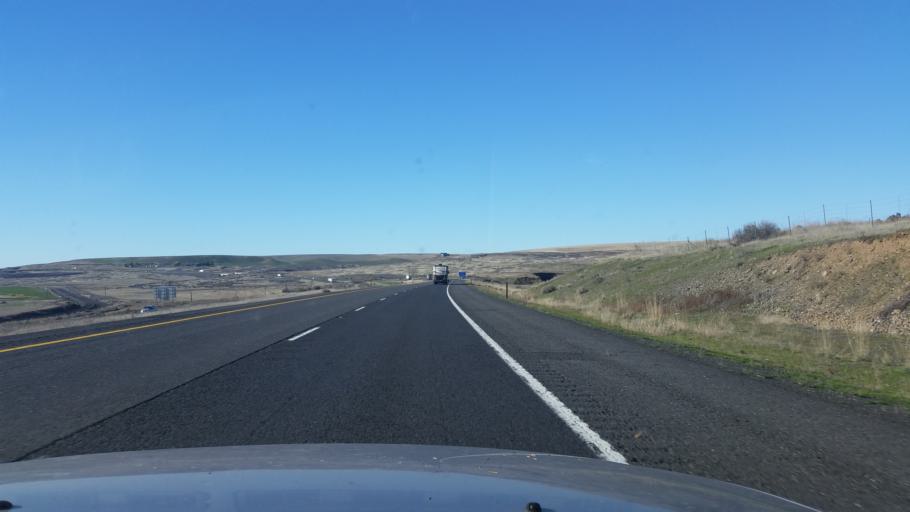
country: US
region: Washington
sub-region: Lincoln County
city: Davenport
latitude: 47.3015
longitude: -118.0034
